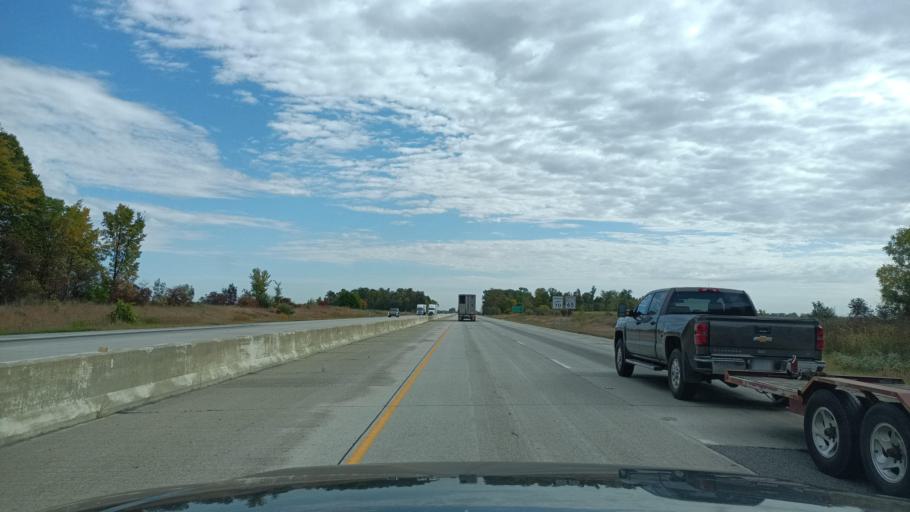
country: US
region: Indiana
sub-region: Wells County
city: Ossian
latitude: 40.9553
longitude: -85.1568
